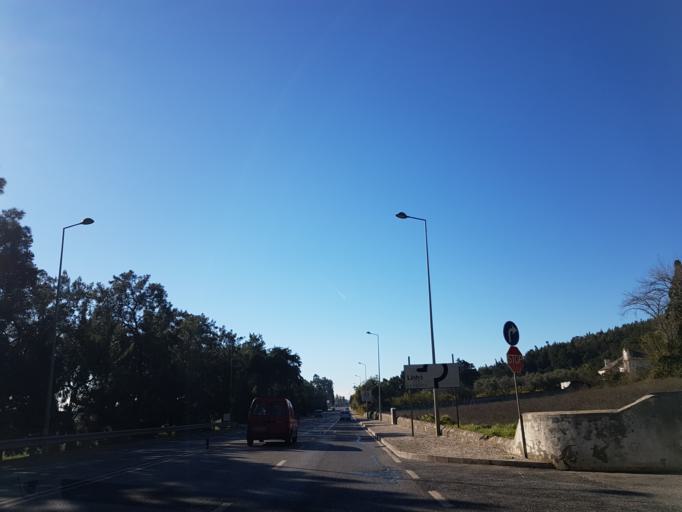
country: PT
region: Lisbon
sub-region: Sintra
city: Sintra
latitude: 38.7781
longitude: -9.3785
